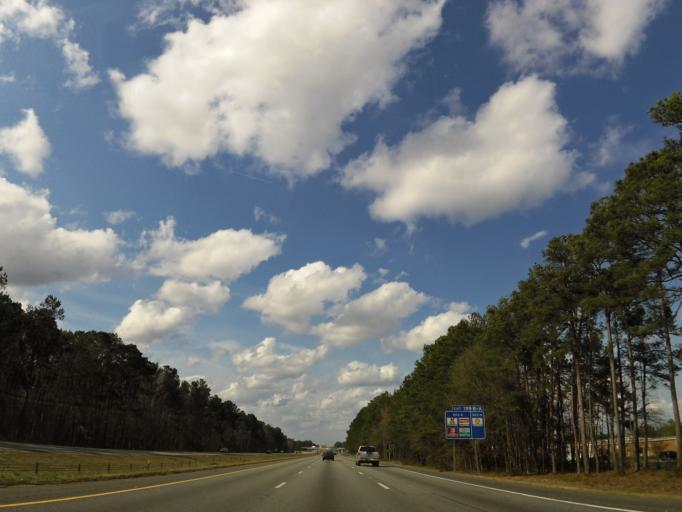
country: US
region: South Carolina
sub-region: Berkeley County
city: Sangaree
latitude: 33.0301
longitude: -80.1402
